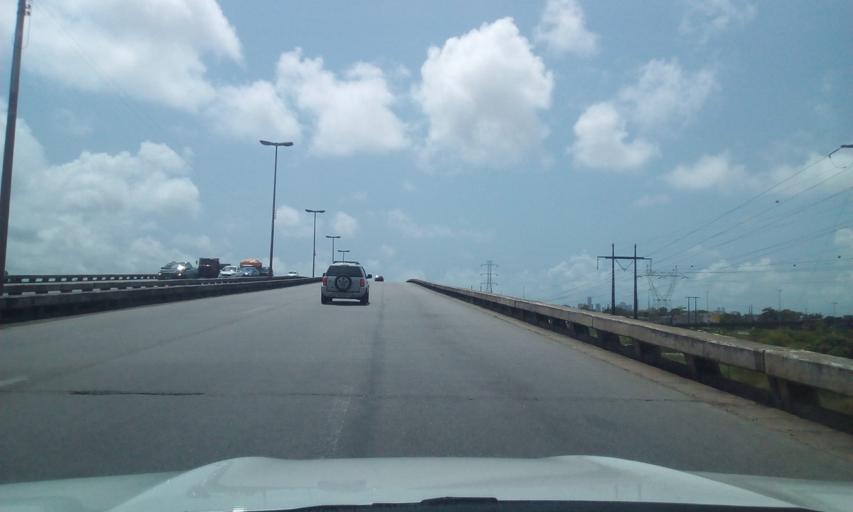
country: BR
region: Pernambuco
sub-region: Recife
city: Recife
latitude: -8.0675
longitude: -34.9440
